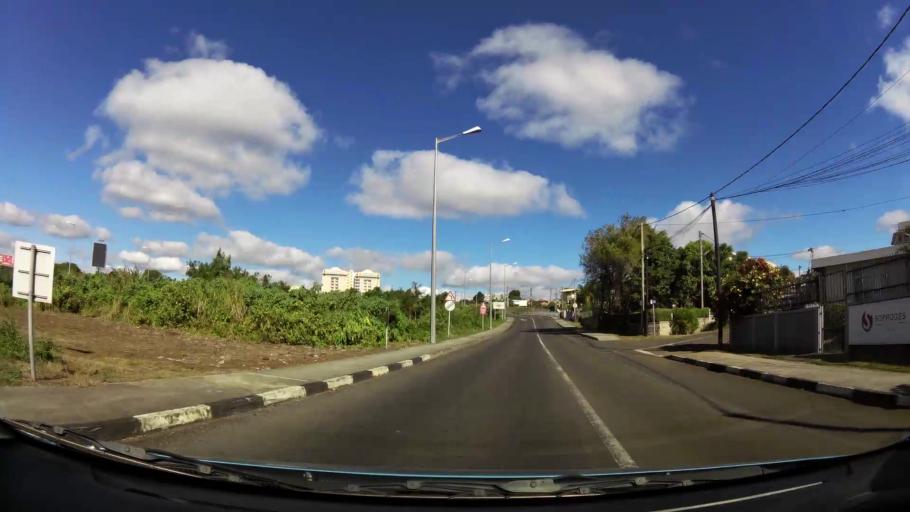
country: MU
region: Plaines Wilhems
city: Quatre Bornes
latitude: -20.2635
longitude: 57.4908
